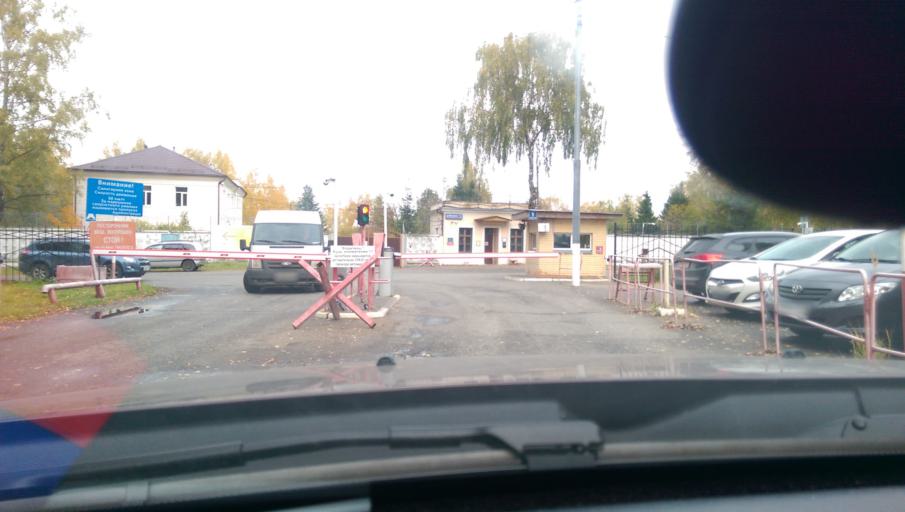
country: RU
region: Moskovskaya
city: Pirogovskiy
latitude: 56.0199
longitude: 37.7304
